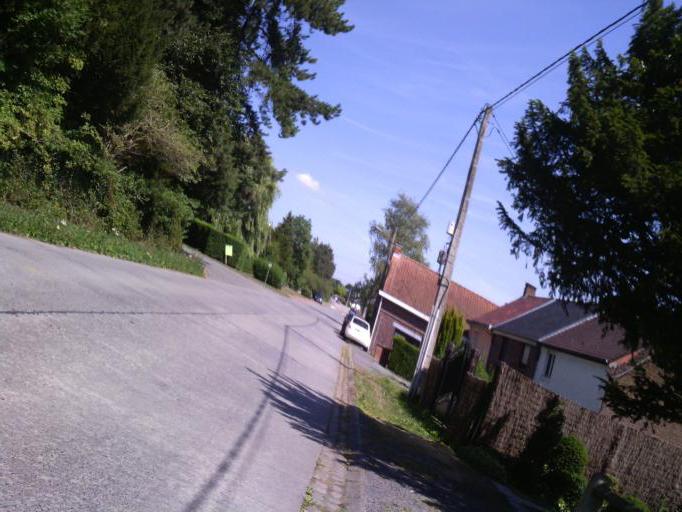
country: BE
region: Wallonia
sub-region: Province du Hainaut
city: Antoing
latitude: 50.6206
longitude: 3.4441
